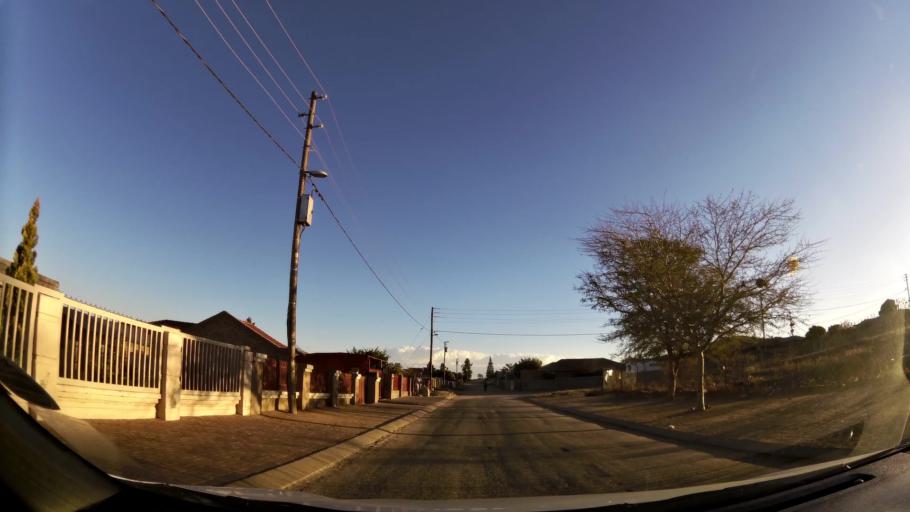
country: ZA
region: Limpopo
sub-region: Capricorn District Municipality
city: Polokwane
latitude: -23.8494
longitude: 29.3536
